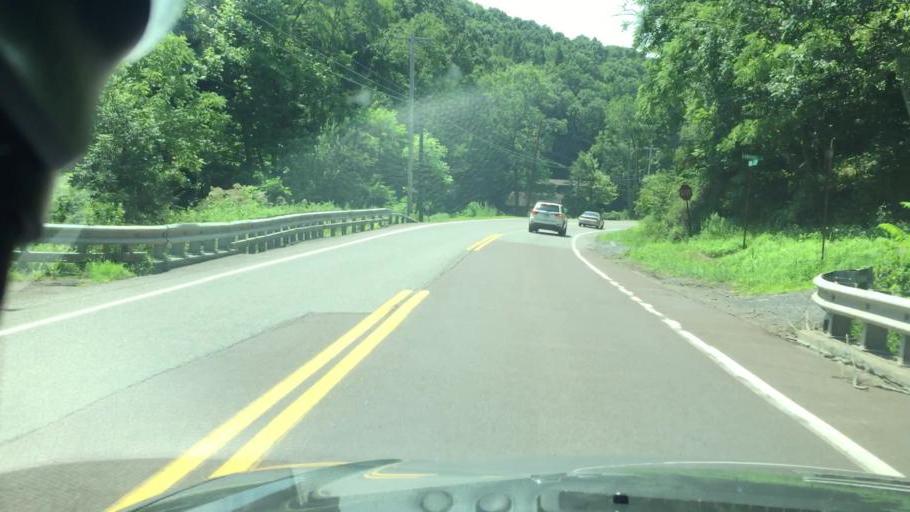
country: US
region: Pennsylvania
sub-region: Columbia County
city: Catawissa
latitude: 40.9137
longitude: -76.4742
